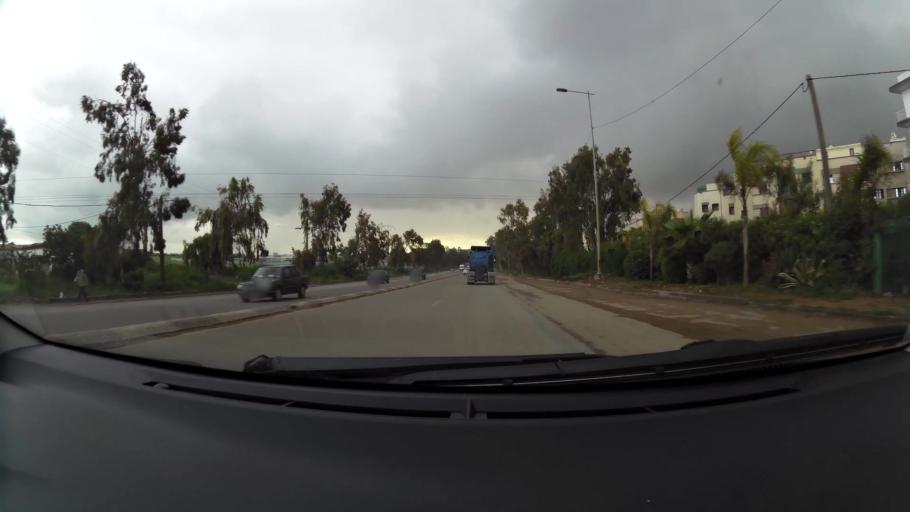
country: MA
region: Grand Casablanca
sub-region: Mediouna
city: Tit Mellil
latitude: 33.5665
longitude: -7.5052
